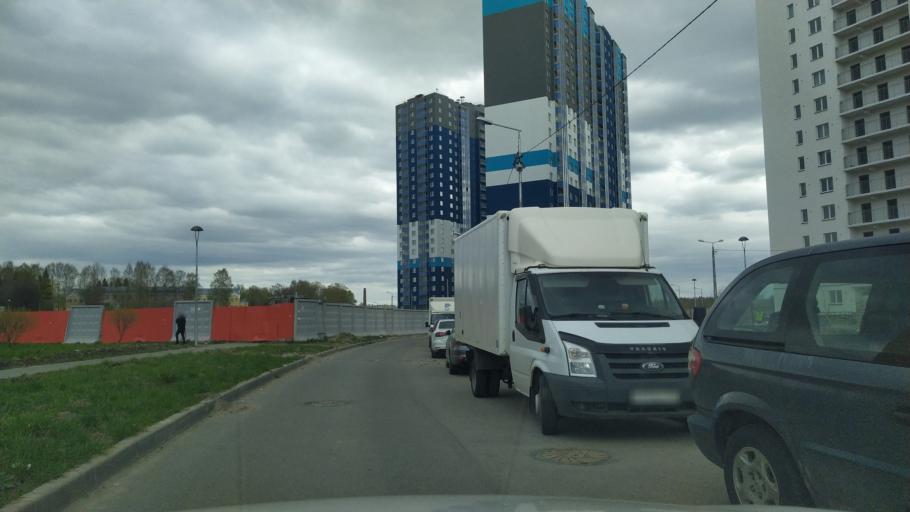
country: RU
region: Leningrad
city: Murino
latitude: 60.0373
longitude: 30.4547
